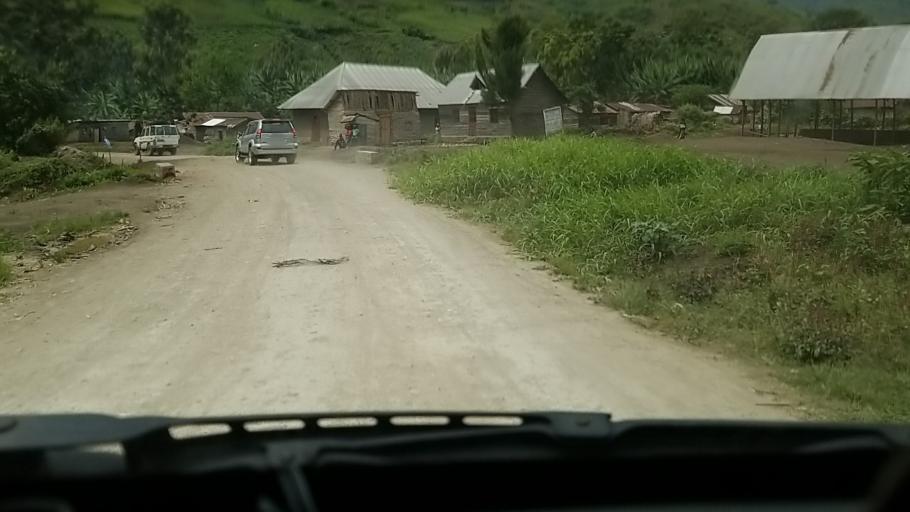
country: CD
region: Nord Kivu
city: Sake
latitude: -1.5910
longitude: 29.0402
